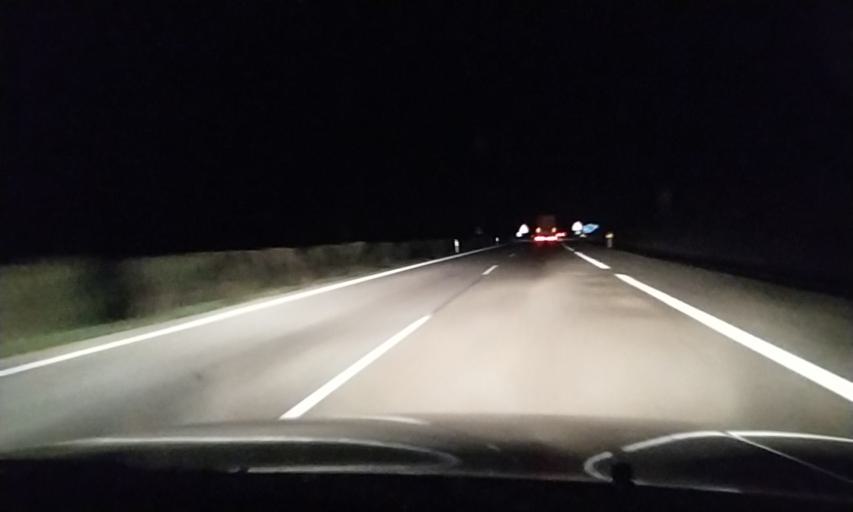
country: ES
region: Castille and Leon
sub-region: Provincia de Zamora
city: Pobladura del Valle
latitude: 42.0998
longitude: -5.7190
